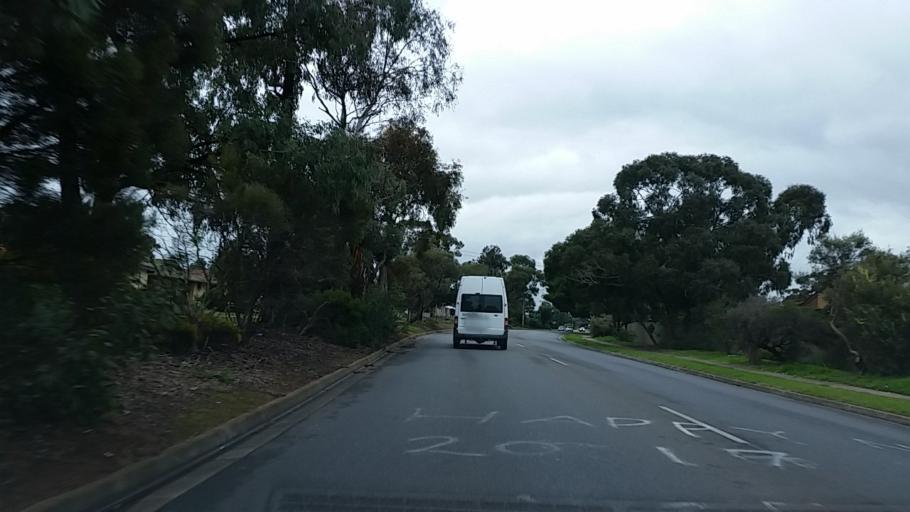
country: AU
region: South Australia
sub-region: Salisbury
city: Salisbury
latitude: -34.7760
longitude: 138.6136
